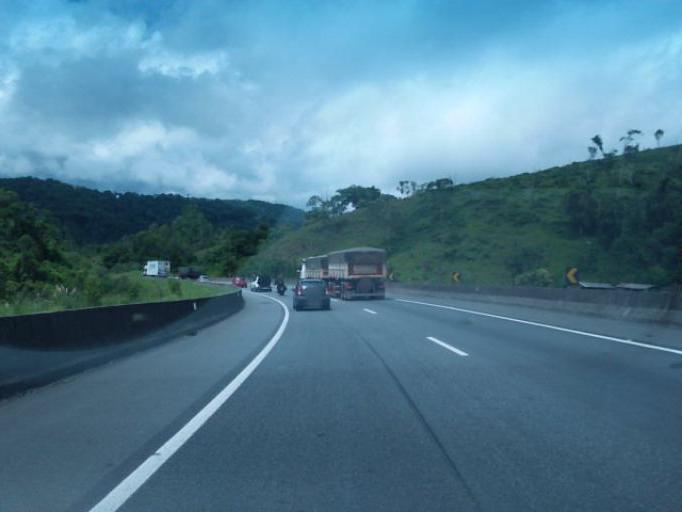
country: BR
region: Parana
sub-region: Antonina
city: Antonina
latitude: -25.0399
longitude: -48.5372
